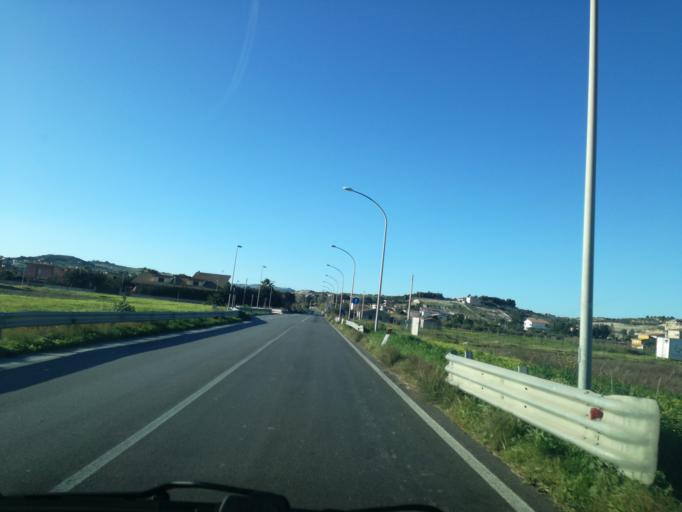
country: IT
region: Sicily
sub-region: Provincia di Caltanissetta
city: Gela
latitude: 37.0974
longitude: 14.1650
